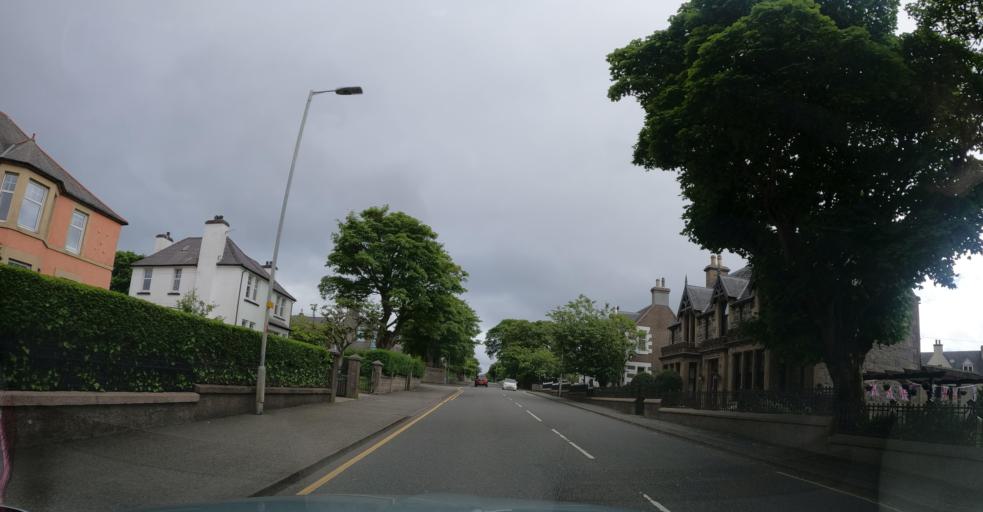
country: GB
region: Scotland
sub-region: Eilean Siar
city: Stornoway
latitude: 58.2131
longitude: -6.3836
